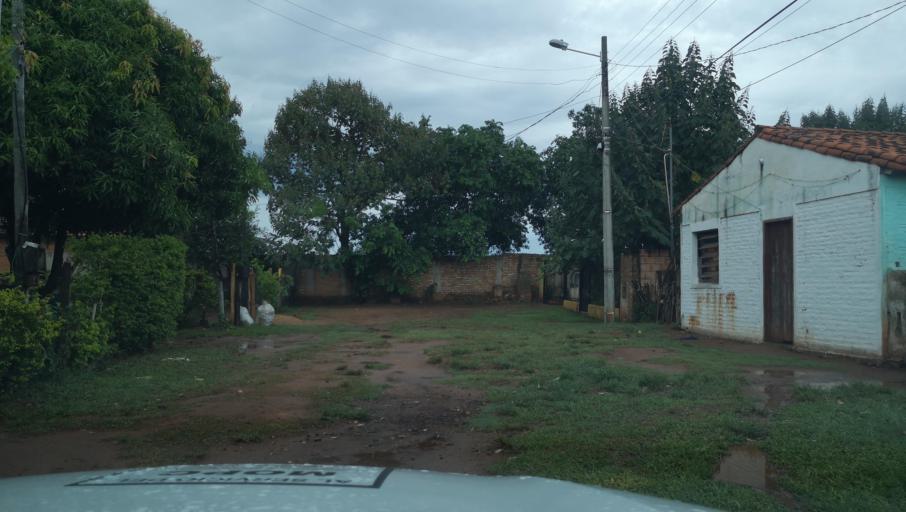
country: PY
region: Misiones
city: Santa Maria
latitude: -26.9002
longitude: -57.0349
